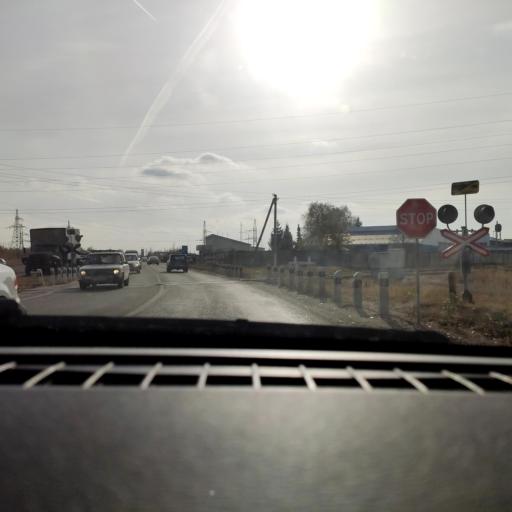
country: RU
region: Voronezj
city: Maslovka
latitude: 51.5898
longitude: 39.2509
